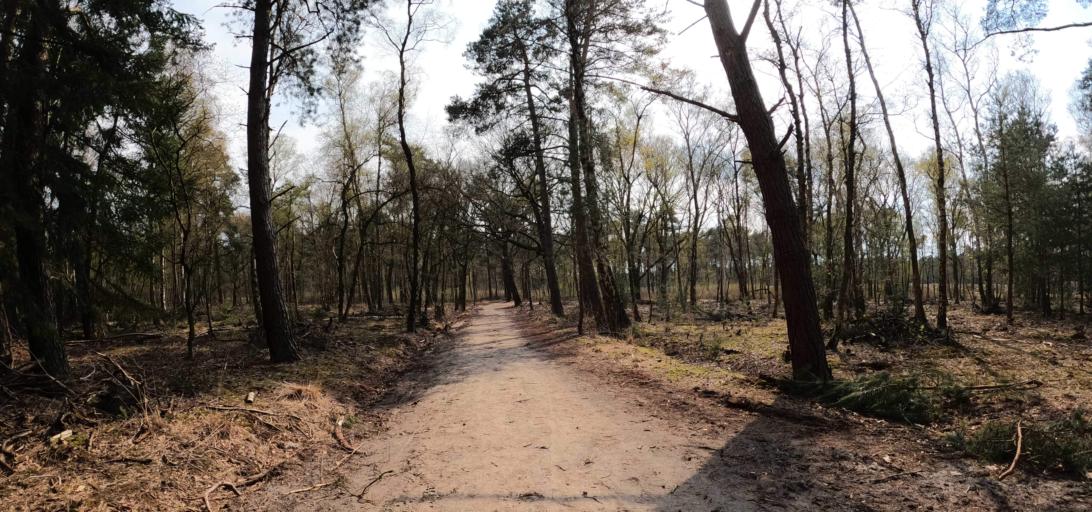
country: BE
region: Flanders
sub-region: Provincie Antwerpen
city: Kalmthout
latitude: 51.4151
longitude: 4.4539
